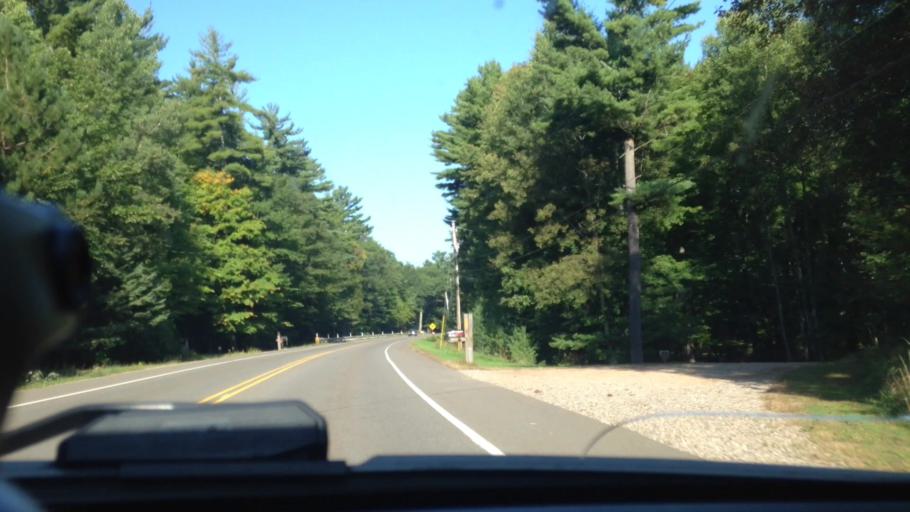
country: US
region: Michigan
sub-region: Dickinson County
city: Quinnesec
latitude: 45.8316
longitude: -88.0026
